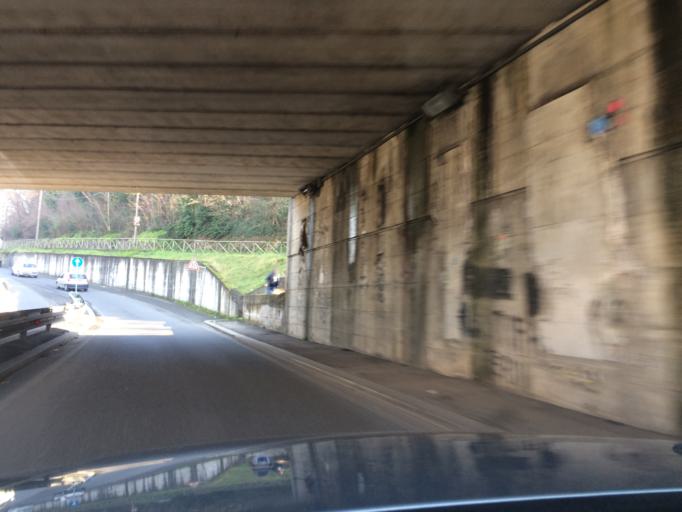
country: IT
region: Umbria
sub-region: Provincia di Terni
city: Terni
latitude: 42.5579
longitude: 12.6545
